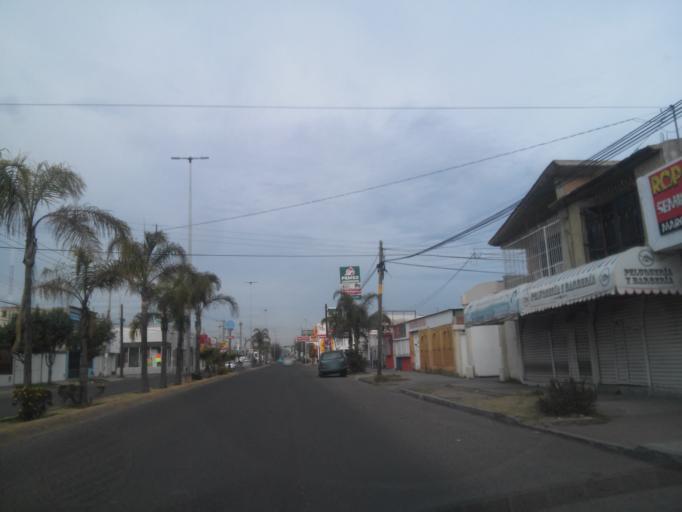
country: MX
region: Durango
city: Victoria de Durango
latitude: 24.0100
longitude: -104.6666
